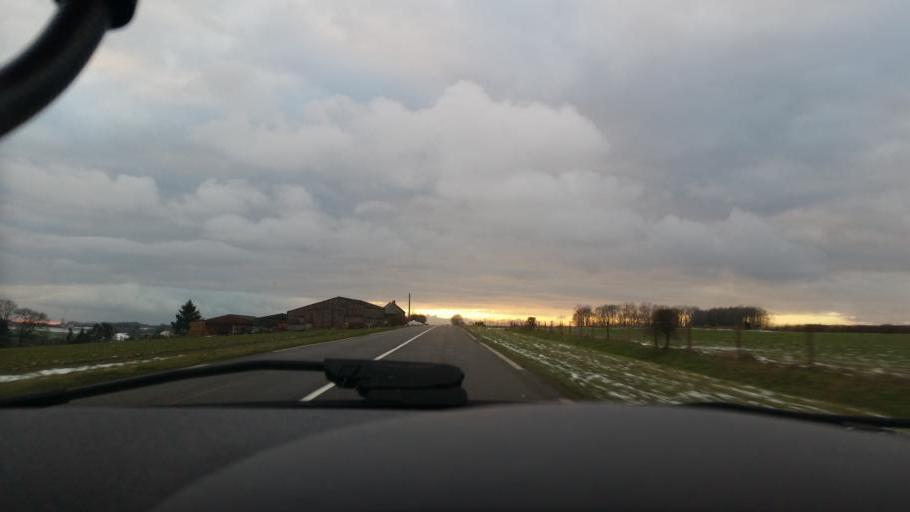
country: FR
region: Nord-Pas-de-Calais
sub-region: Departement du Nord
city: Jeumont
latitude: 50.2506
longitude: 4.1207
